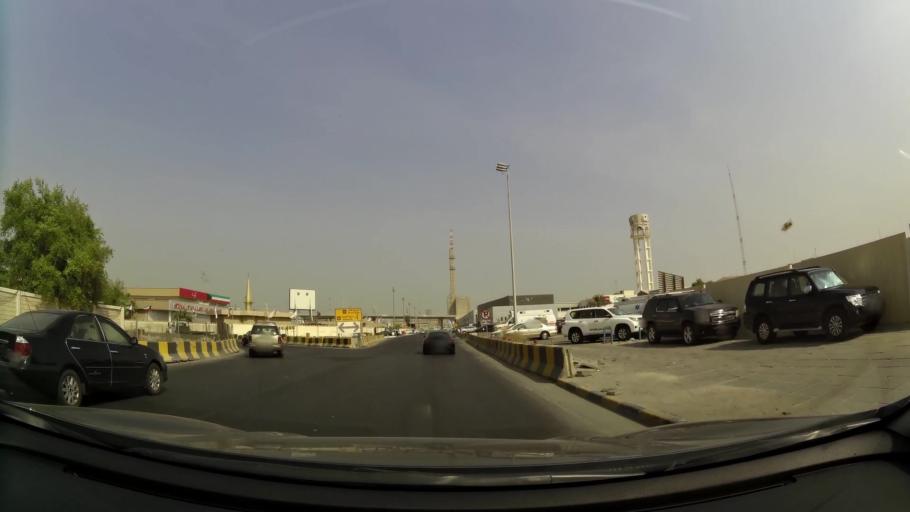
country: KW
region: Al Asimah
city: Ash Shamiyah
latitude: 29.3372
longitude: 47.9429
